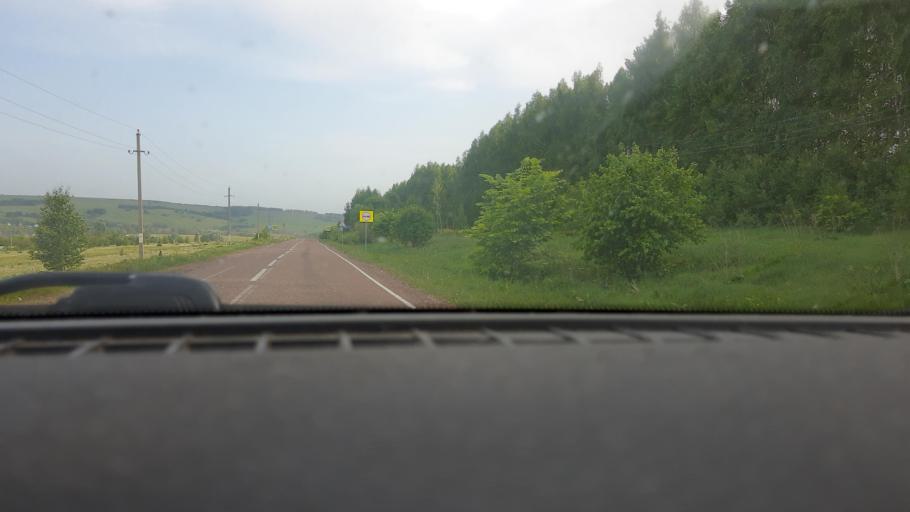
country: RU
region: Bashkortostan
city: Ulukulevo
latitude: 54.5585
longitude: 56.4349
